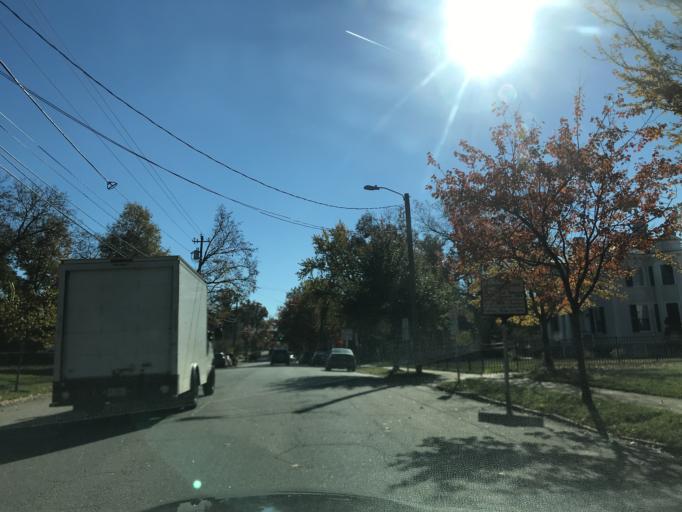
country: US
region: North Carolina
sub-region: Wake County
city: Raleigh
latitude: 35.7873
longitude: -78.6361
